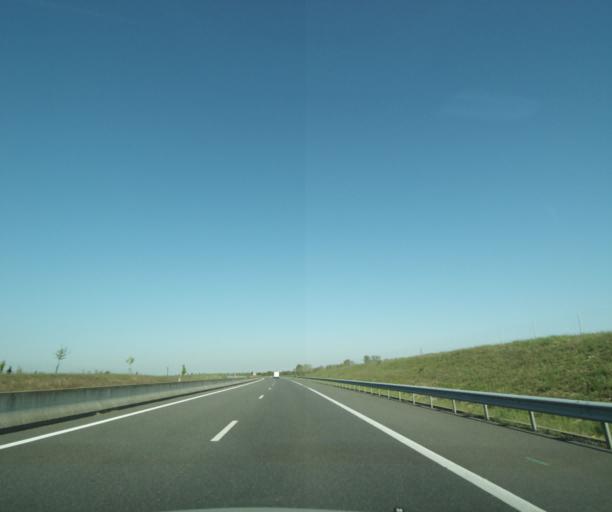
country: FR
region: Centre
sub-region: Departement du Loiret
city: Beaune-la-Rolande
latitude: 48.0929
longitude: 2.4210
